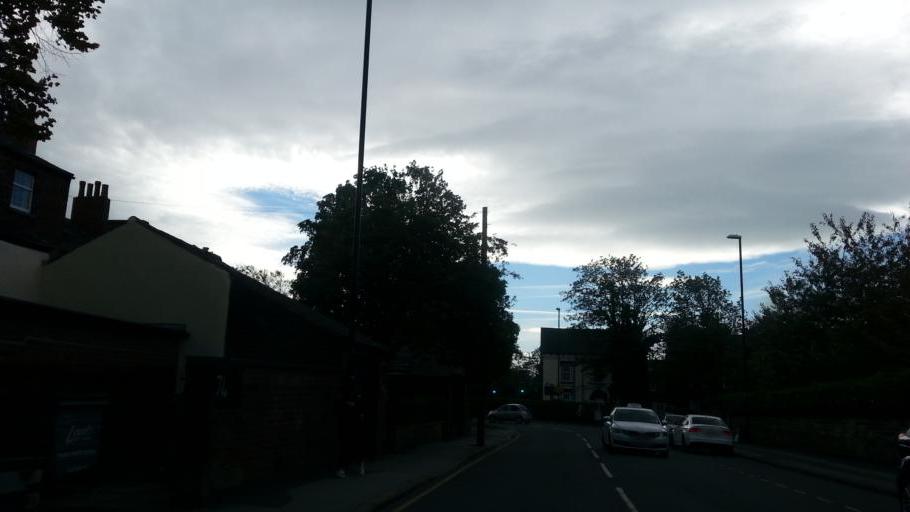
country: GB
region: England
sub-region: City and Borough of Leeds
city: Leeds
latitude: 53.8071
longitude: -1.5602
